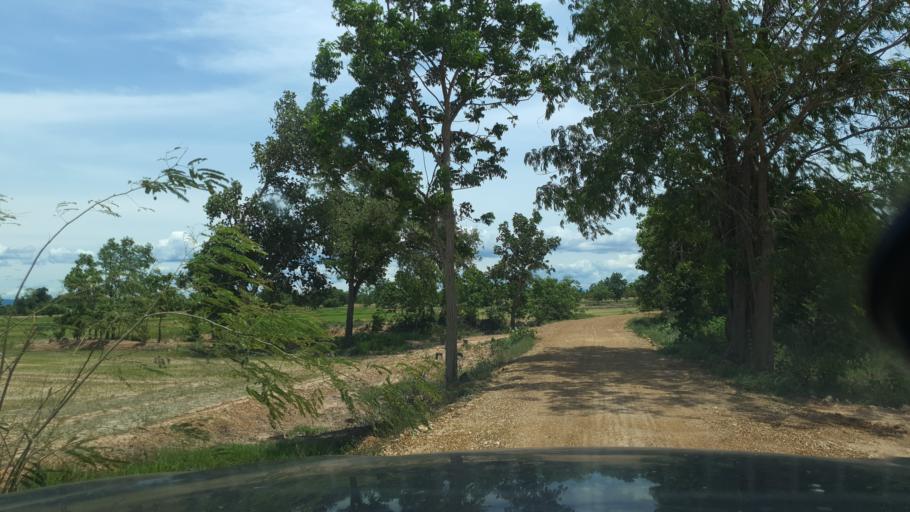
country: TH
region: Sukhothai
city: Ban Na
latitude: 17.1323
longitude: 99.6702
